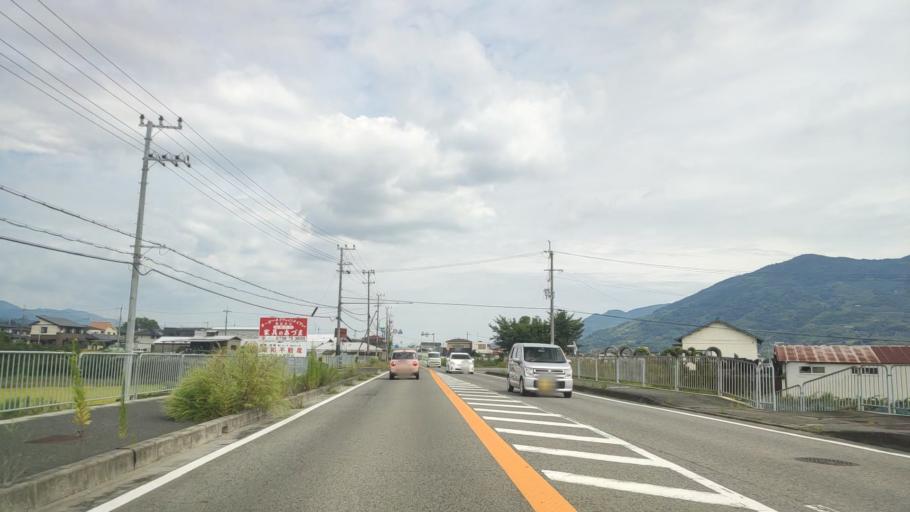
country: JP
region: Wakayama
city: Hashimoto
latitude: 34.2862
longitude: 135.4705
